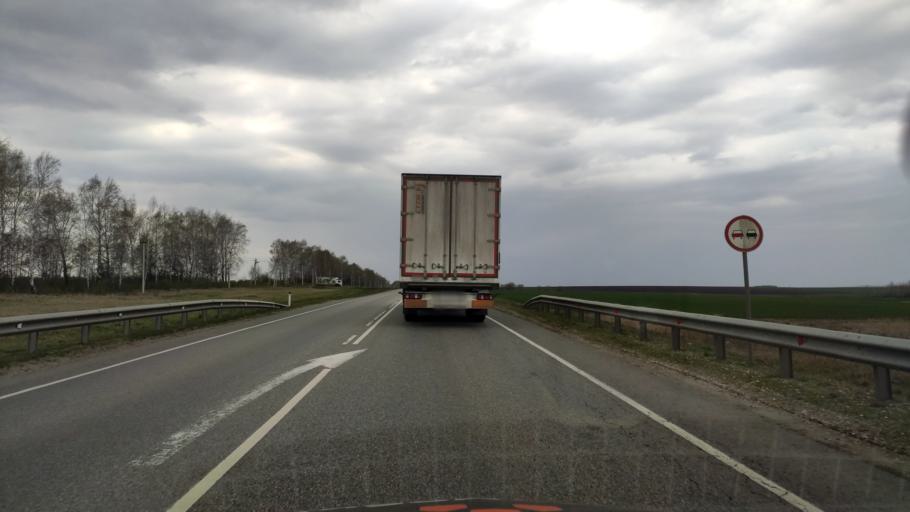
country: RU
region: Kursk
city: Gorshechnoye
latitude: 51.5487
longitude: 38.1209
